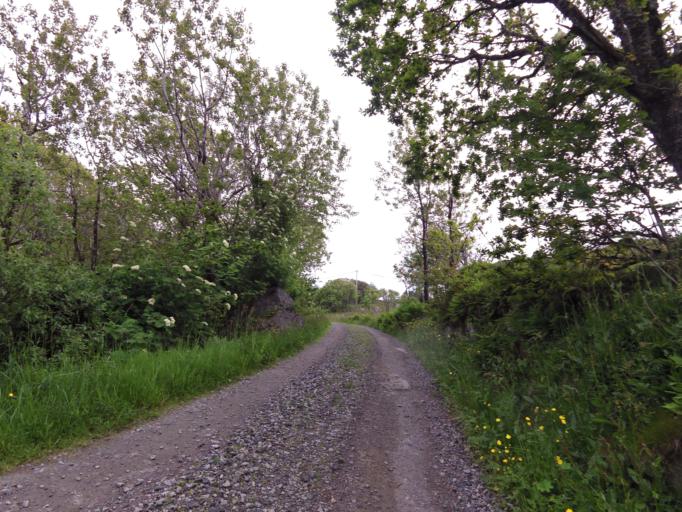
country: NO
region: Vest-Agder
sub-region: Farsund
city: Vestbygd
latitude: 58.1530
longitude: 6.6223
